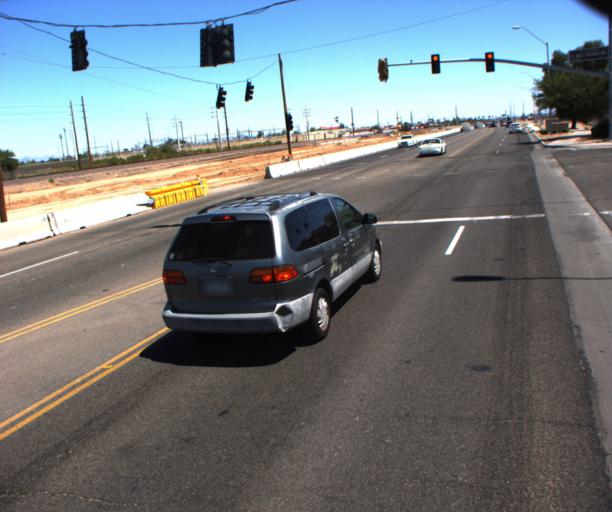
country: US
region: Arizona
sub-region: Maricopa County
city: Surprise
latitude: 33.6363
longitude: -112.3476
